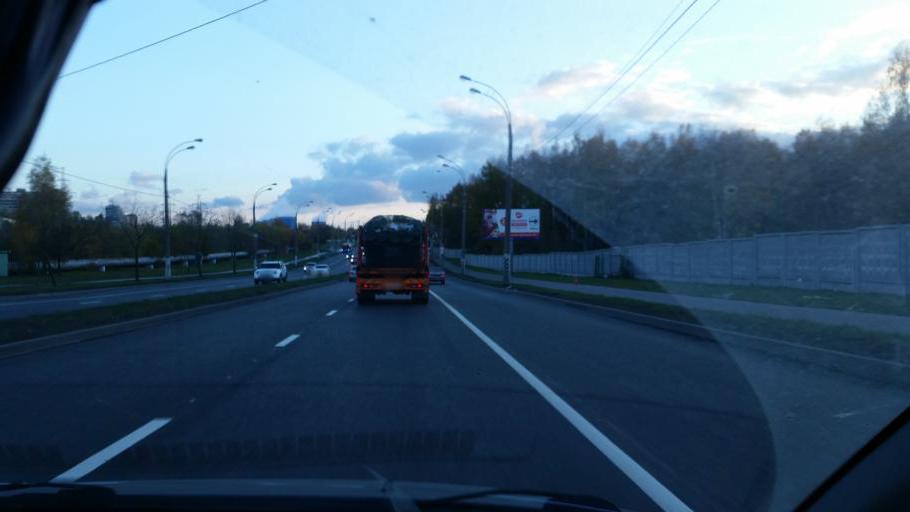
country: RU
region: Moskovskaya
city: Biryulevo Zapadnoye
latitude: 55.5962
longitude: 37.6360
